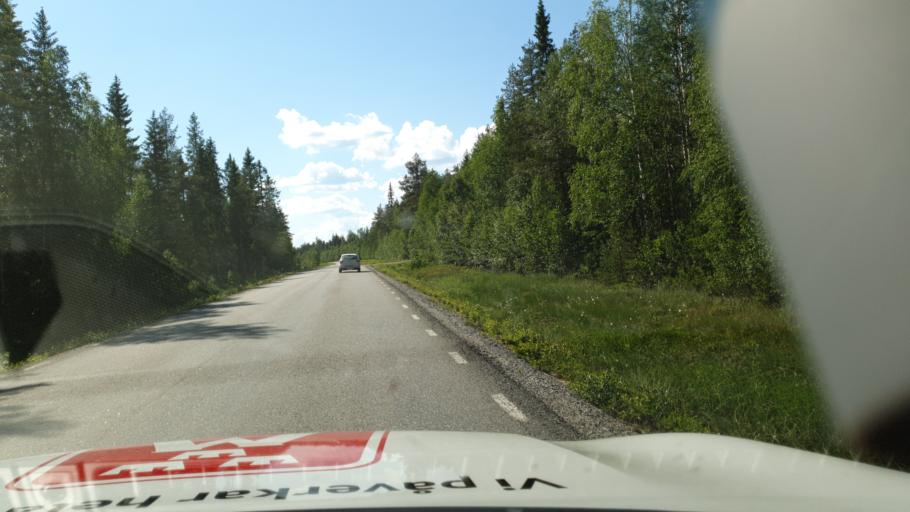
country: SE
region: Vaesterbotten
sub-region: Vindelns Kommun
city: Vindeln
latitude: 64.2559
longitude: 19.8828
